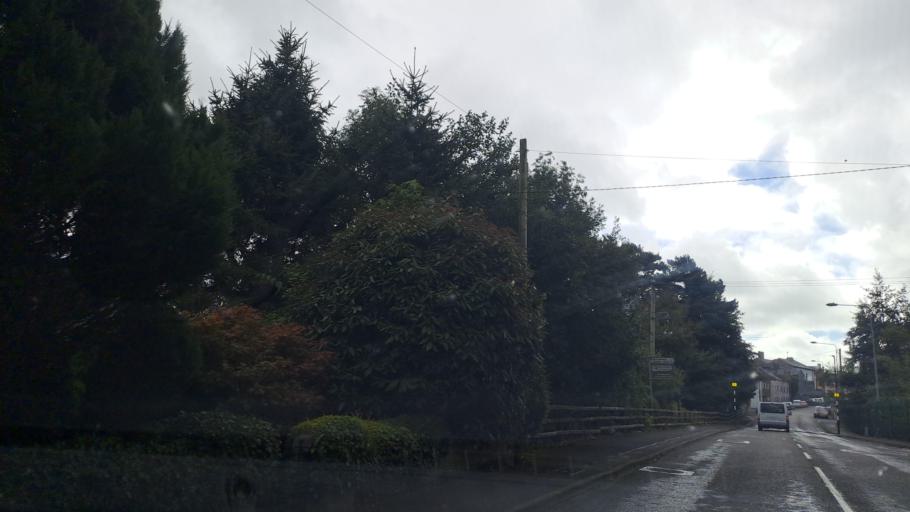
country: IE
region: Ulster
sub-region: An Cabhan
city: Bailieborough
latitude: 53.9195
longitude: -6.9706
